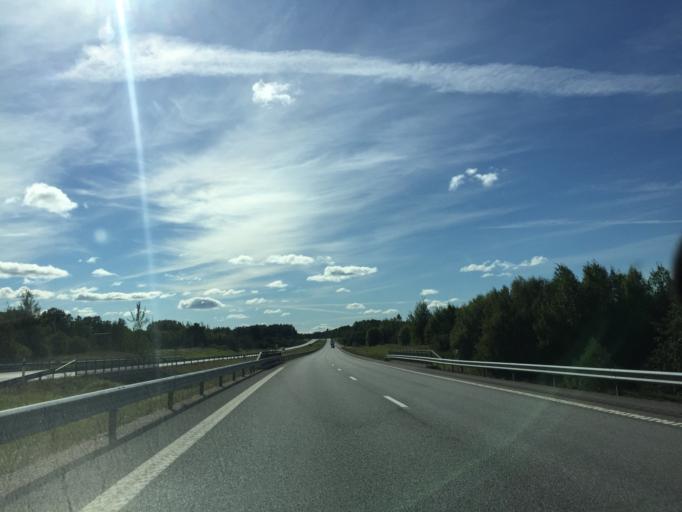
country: SE
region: Vaestmanland
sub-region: Kopings Kommun
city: Koping
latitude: 59.5012
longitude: 15.9337
